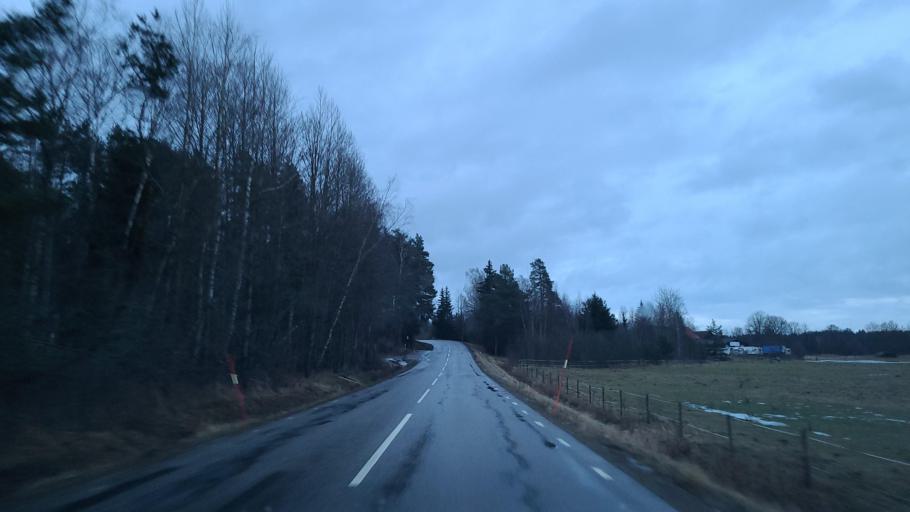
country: SE
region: Stockholm
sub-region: Norrtalje Kommun
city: Norrtalje
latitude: 59.7318
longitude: 18.5757
